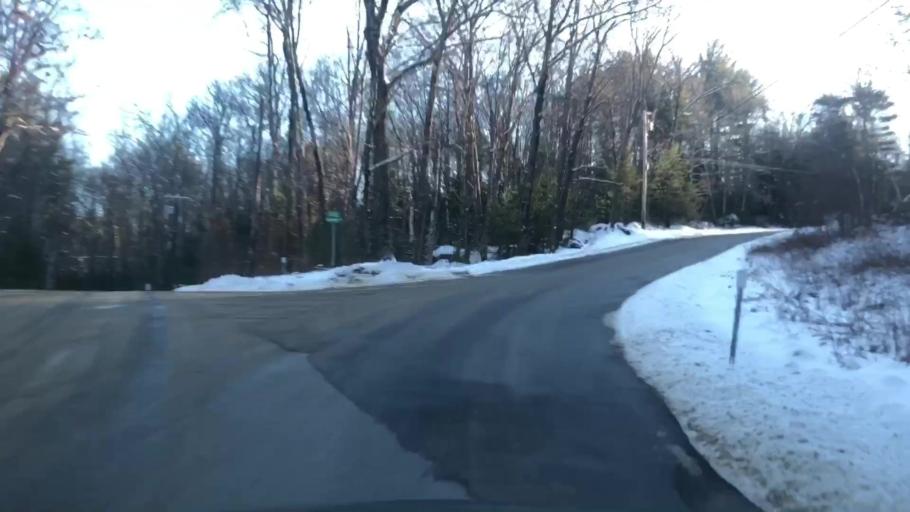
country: US
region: New Hampshire
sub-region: Hillsborough County
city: Milford
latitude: 42.8075
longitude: -71.6678
